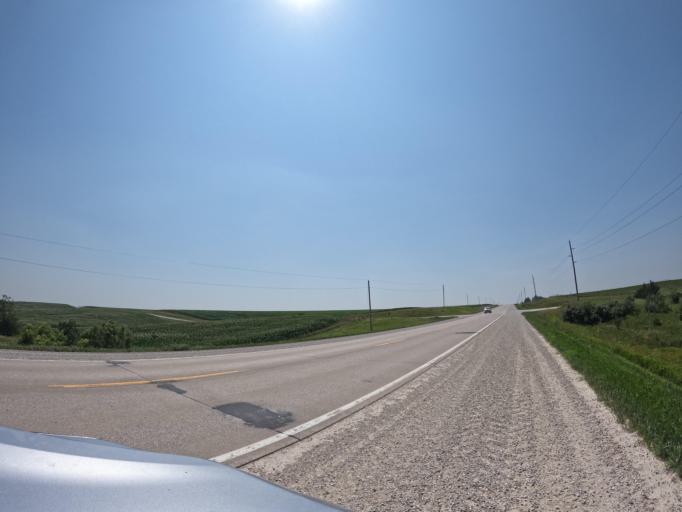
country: US
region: Iowa
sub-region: Keokuk County
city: Sigourney
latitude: 41.3369
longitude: -92.2570
